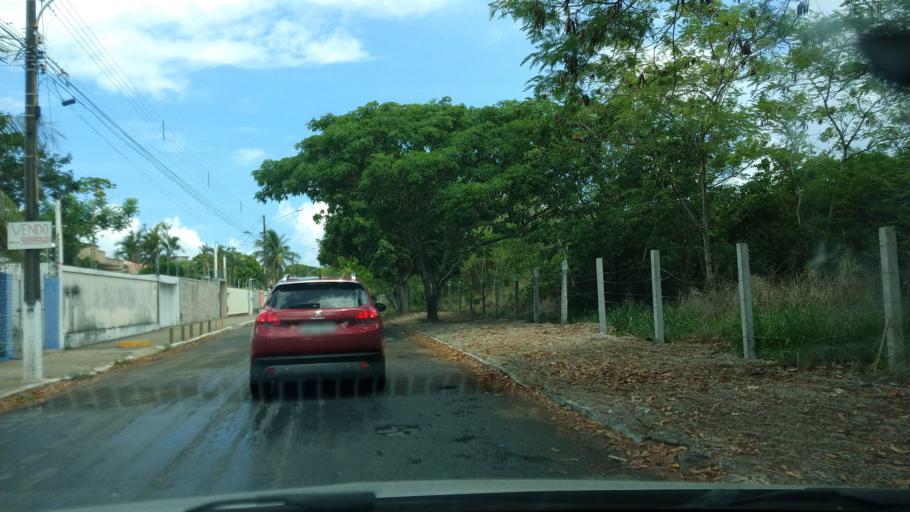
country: BR
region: Rio Grande do Norte
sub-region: Natal
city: Natal
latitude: -5.8490
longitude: -35.1978
